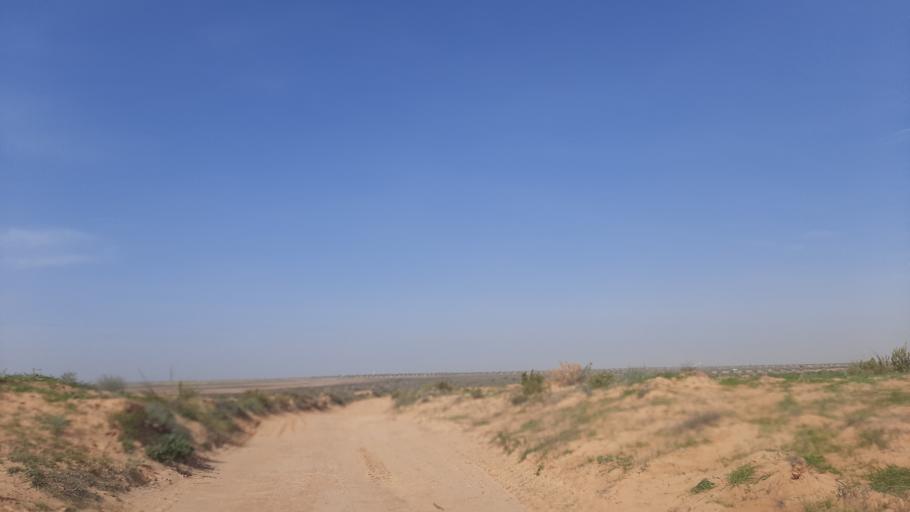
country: TN
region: Madanin
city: Zarzis
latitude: 33.4379
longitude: 10.8072
